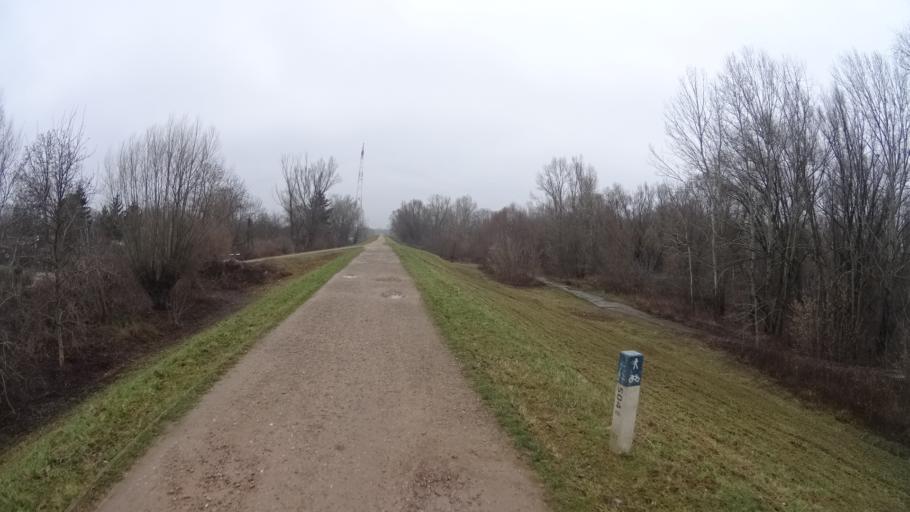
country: PL
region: Masovian Voivodeship
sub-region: Warszawa
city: Wilanow
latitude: 52.1945
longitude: 21.1010
